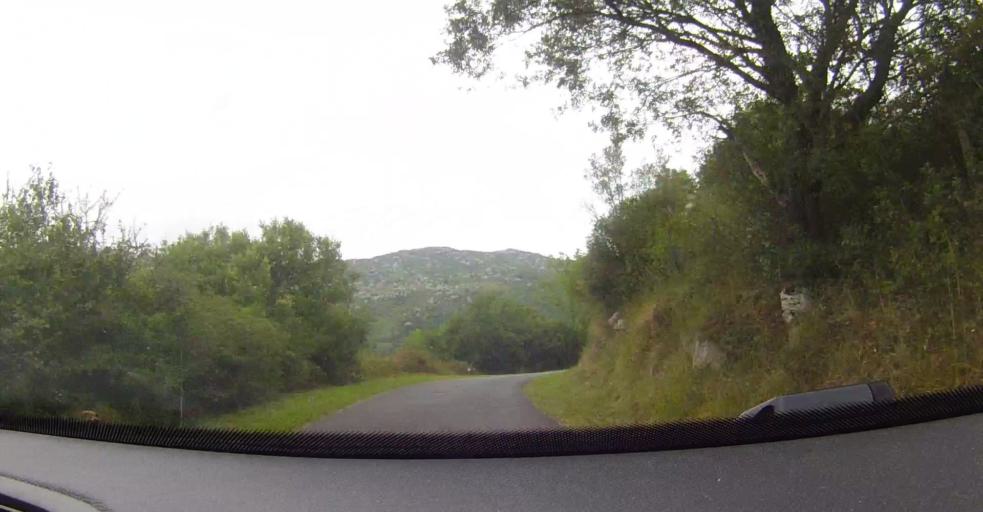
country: ES
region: Cantabria
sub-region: Provincia de Cantabria
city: Rasines
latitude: 43.2619
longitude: -3.3753
